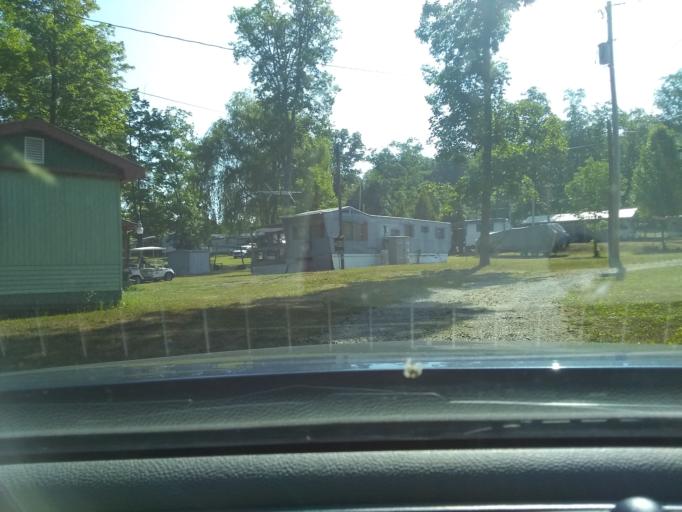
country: US
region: Pennsylvania
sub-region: Cambria County
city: Patton
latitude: 40.6558
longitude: -78.5116
